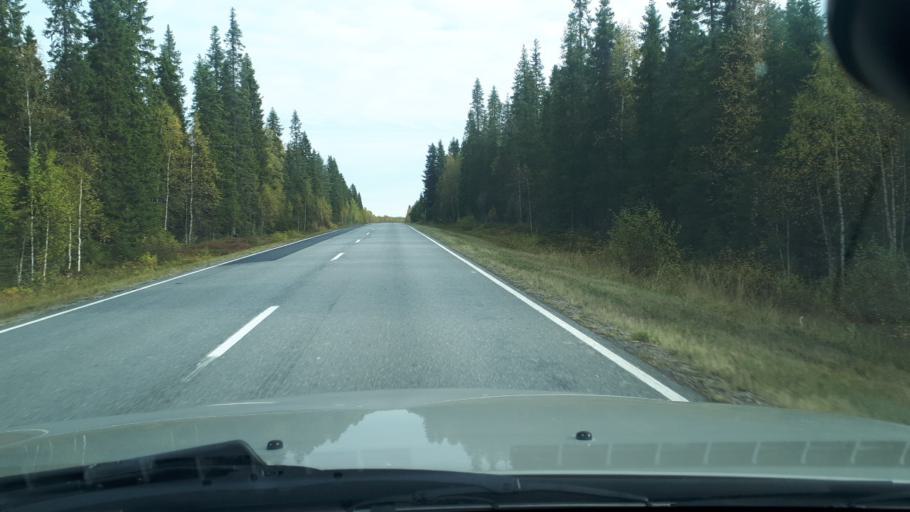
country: FI
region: Lapland
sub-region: Rovaniemi
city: Ranua
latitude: 65.9745
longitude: 26.1127
